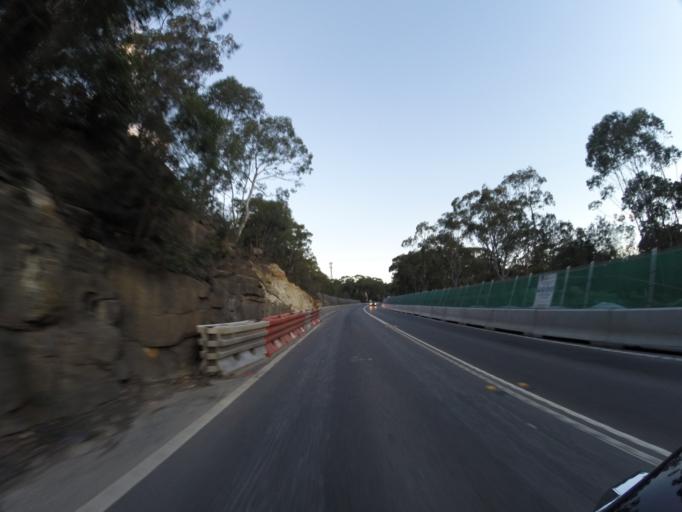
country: AU
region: New South Wales
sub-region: Liverpool
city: East Hills
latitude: -33.9828
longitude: 150.9927
